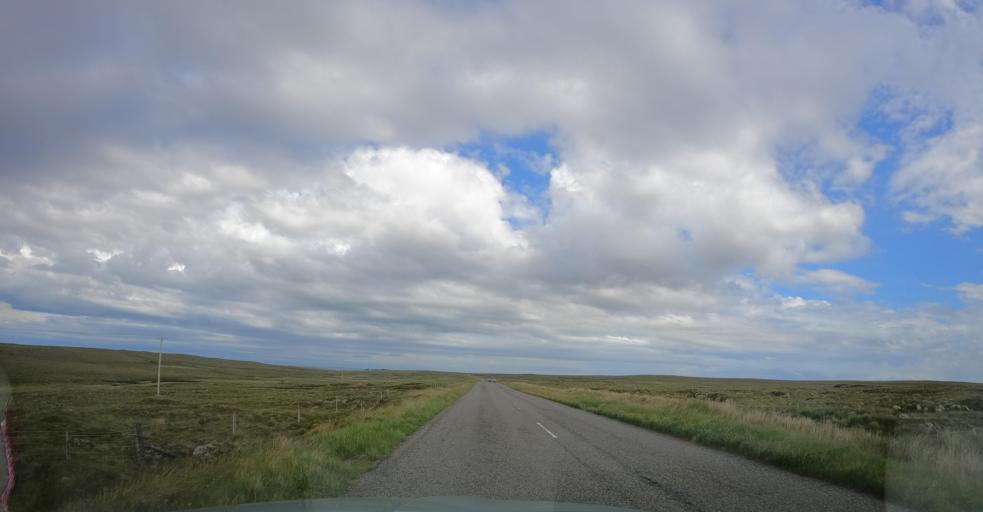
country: GB
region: Scotland
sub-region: Eilean Siar
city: Isle of Lewis
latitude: 58.3132
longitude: -6.4568
